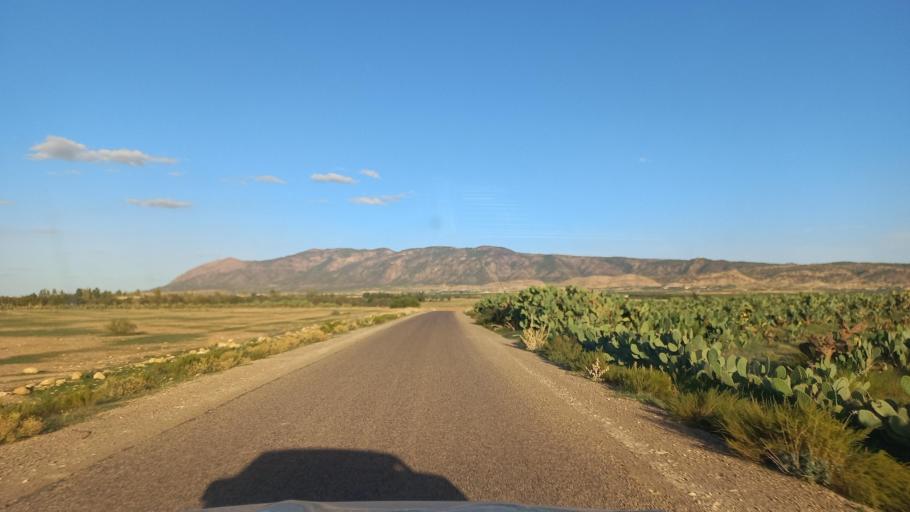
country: TN
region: Al Qasrayn
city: Sbiba
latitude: 35.4113
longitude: 9.1425
